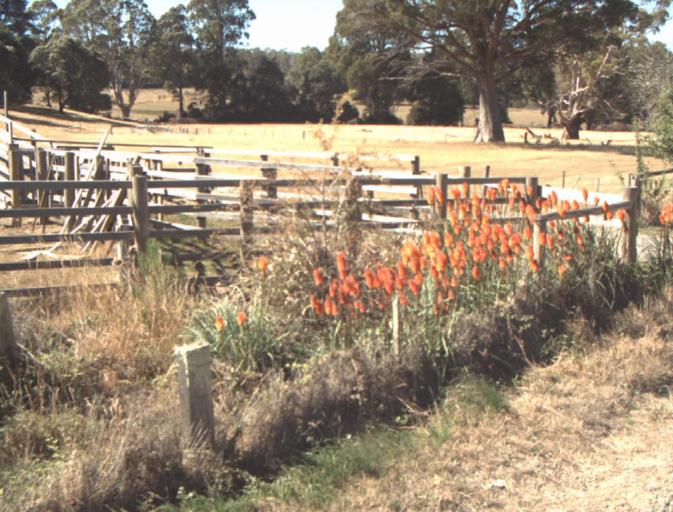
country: AU
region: Tasmania
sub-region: Launceston
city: Newstead
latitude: -41.3157
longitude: 147.3203
